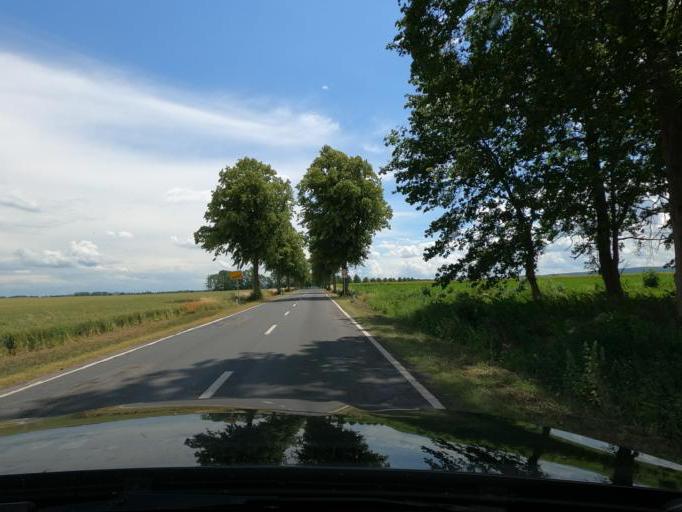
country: DE
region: Lower Saxony
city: Schellerten
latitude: 52.1938
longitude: 10.0357
